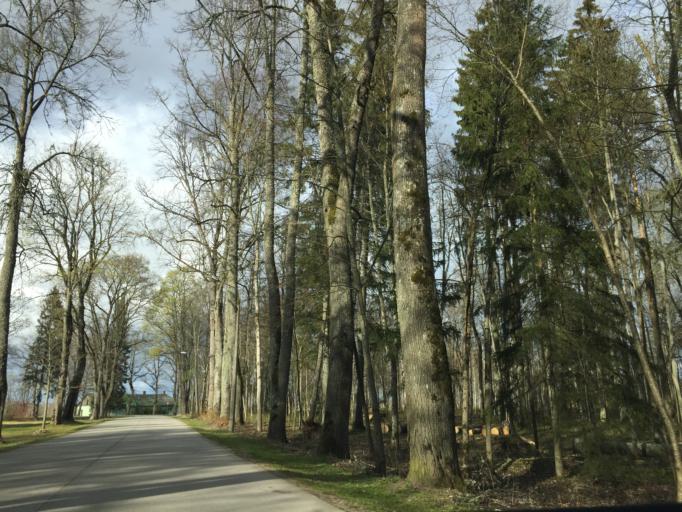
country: LV
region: Burtnieki
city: Matisi
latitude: 57.5957
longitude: 25.0810
